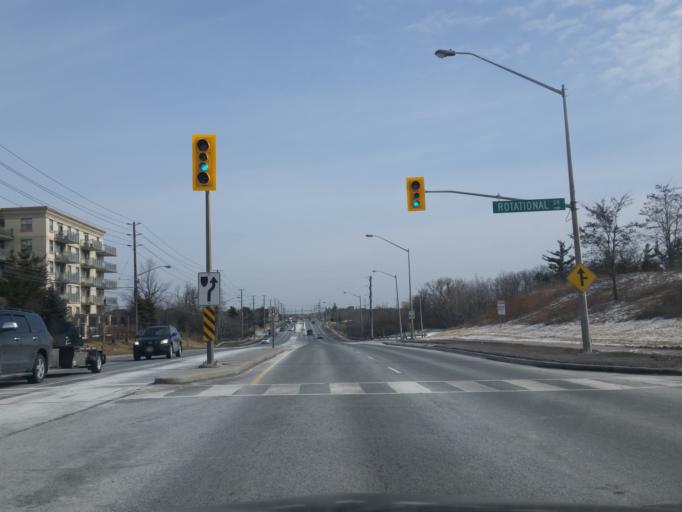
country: CA
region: Ontario
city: Vaughan
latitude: 43.8345
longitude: -79.5172
